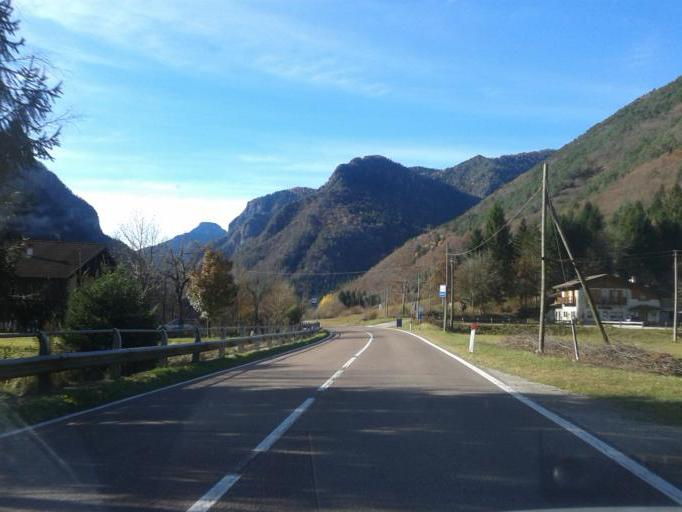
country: IT
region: Trentino-Alto Adige
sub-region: Provincia di Trento
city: Cimego
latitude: 45.8761
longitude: 10.6590
